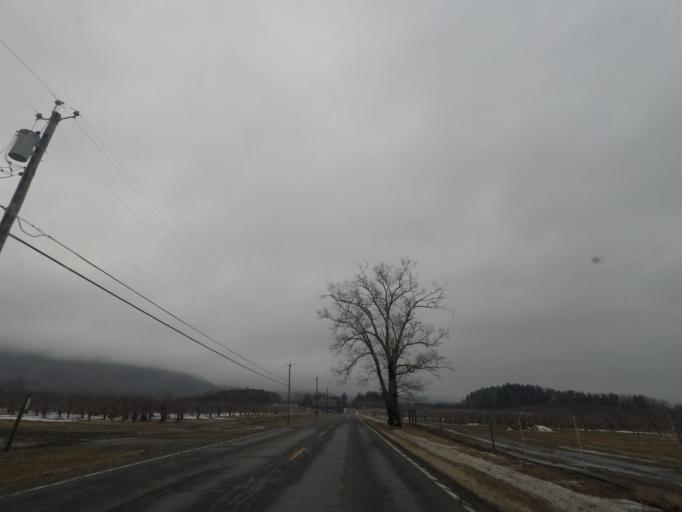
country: US
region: New York
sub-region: Albany County
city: Voorheesville
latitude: 42.6547
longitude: -73.9681
